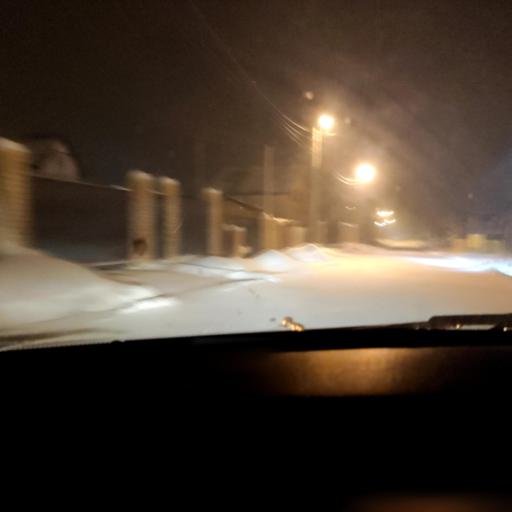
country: RU
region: Perm
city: Kultayevo
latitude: 57.8576
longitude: 55.9231
